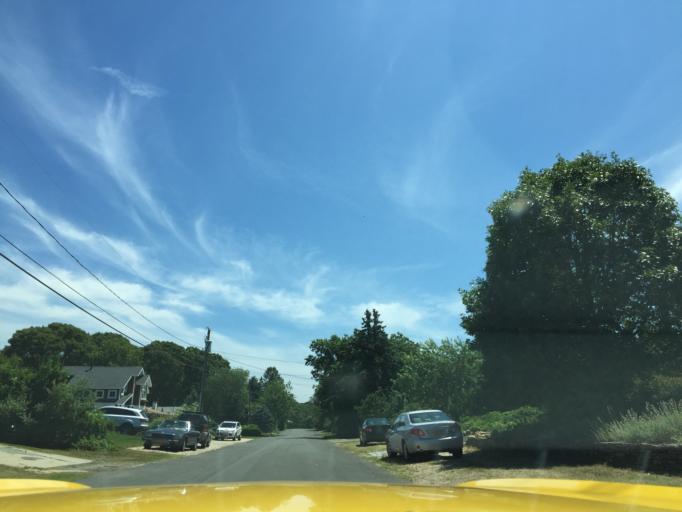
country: US
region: New York
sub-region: Suffolk County
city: Montauk
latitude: 41.0694
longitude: -71.9484
